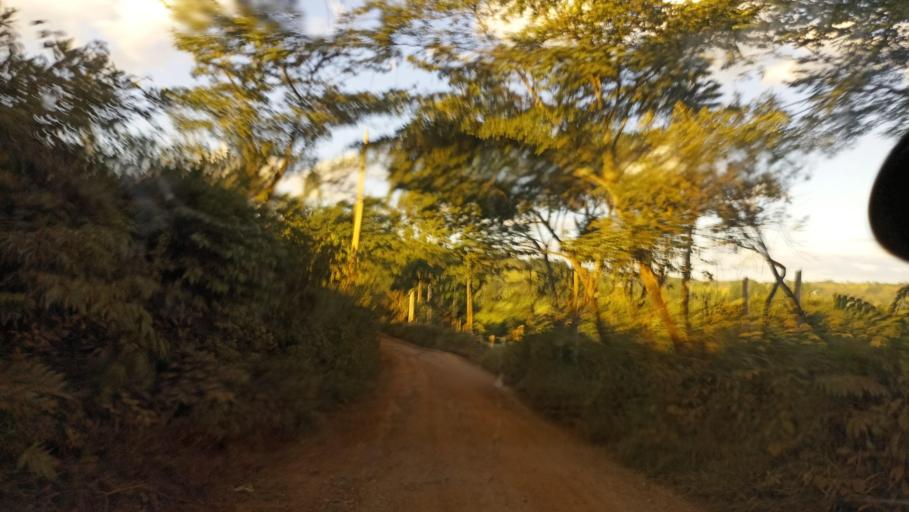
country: BR
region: Minas Gerais
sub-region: Sao Joao Del Rei
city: Sao Joao del Rei
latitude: -21.1836
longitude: -44.3464
